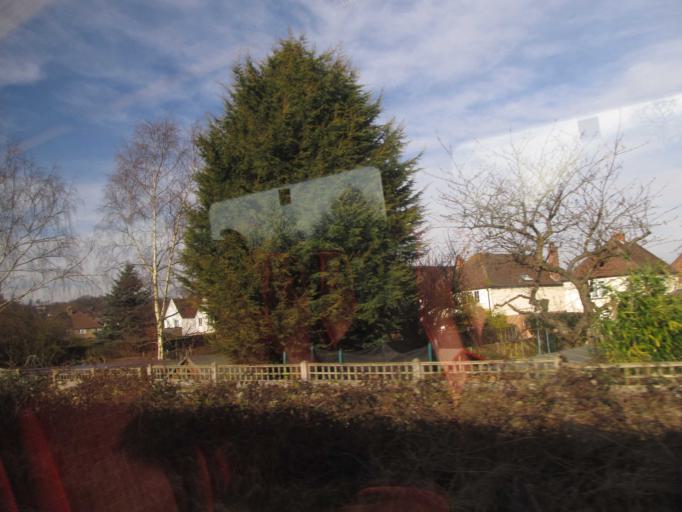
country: GB
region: England
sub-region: Surrey
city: Godalming
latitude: 51.1999
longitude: -0.6006
